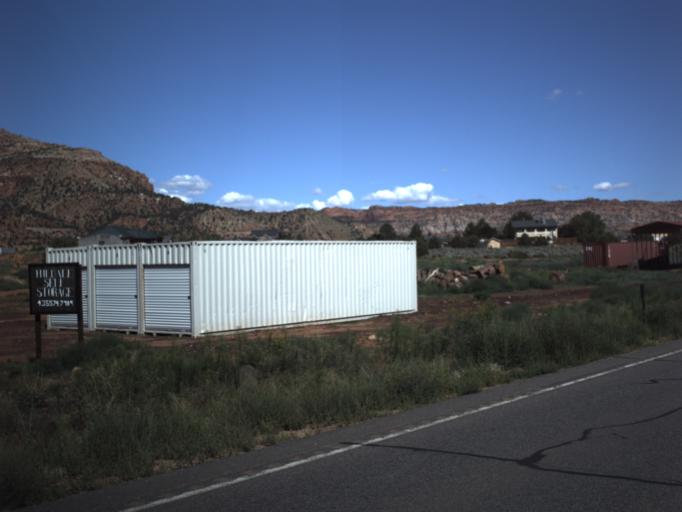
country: US
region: Arizona
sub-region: Mohave County
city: Colorado City
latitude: 37.0052
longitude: -113.0047
